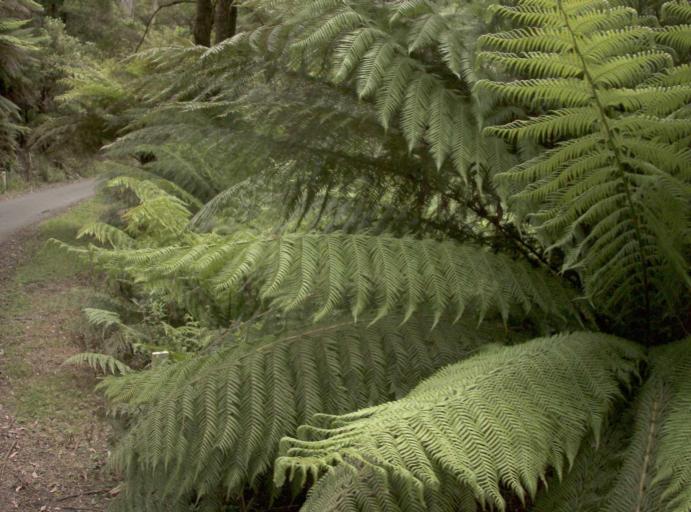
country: AU
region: Victoria
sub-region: Latrobe
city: Traralgon
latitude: -38.4482
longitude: 146.5356
